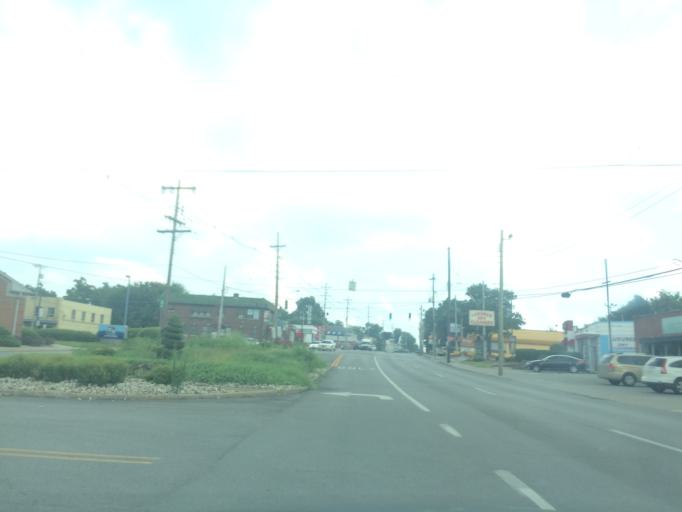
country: US
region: Kentucky
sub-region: Jefferson County
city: Audubon Park
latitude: 38.2136
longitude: -85.7421
